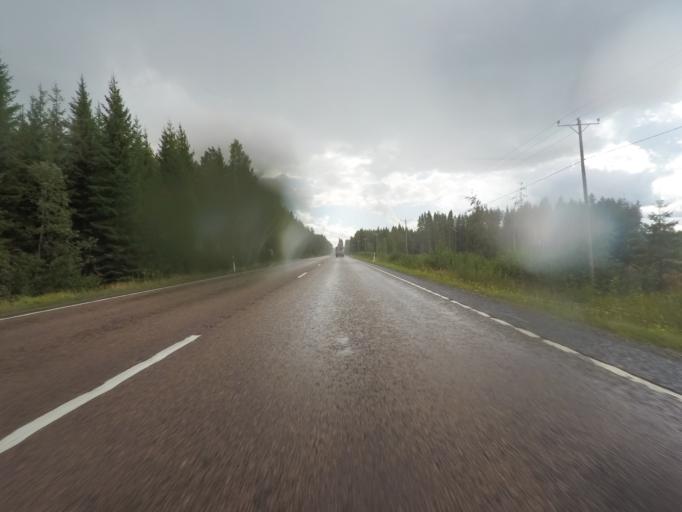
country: FI
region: Central Finland
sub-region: Joutsa
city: Leivonmaeki
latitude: 61.9301
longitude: 26.1150
